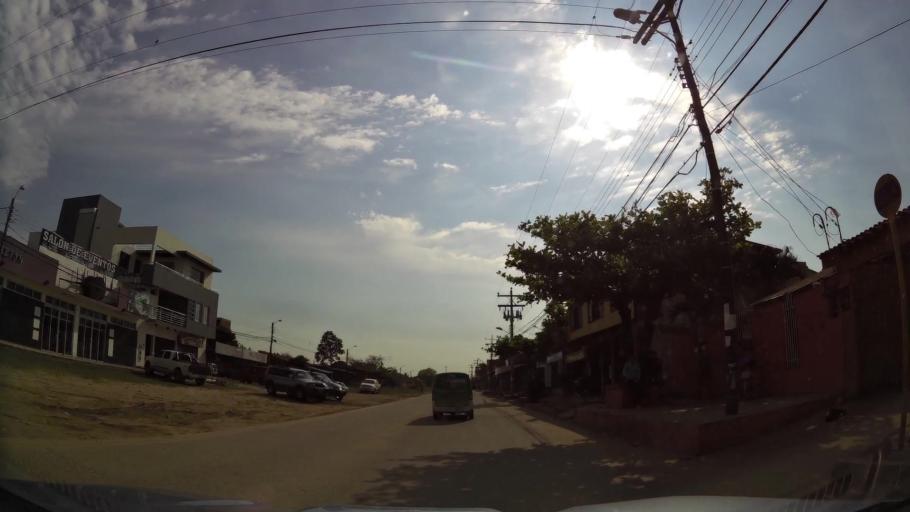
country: BO
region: Santa Cruz
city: Santa Cruz de la Sierra
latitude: -17.7324
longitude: -63.1422
